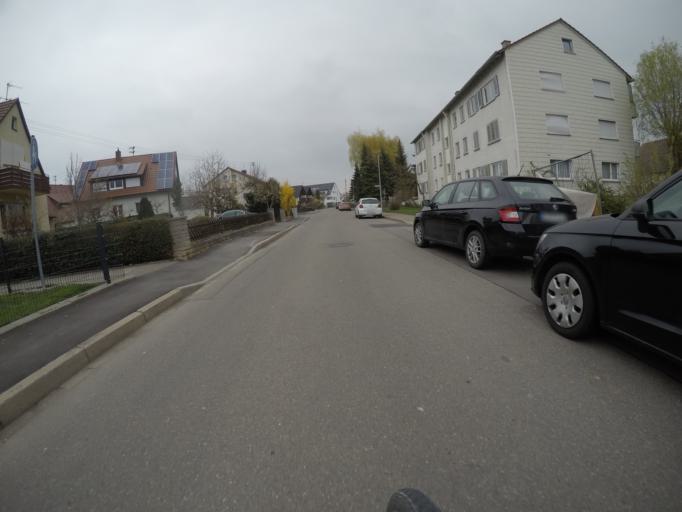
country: DE
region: Baden-Wuerttemberg
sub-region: Regierungsbezirk Stuttgart
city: Nufringen
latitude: 48.6207
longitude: 8.8930
